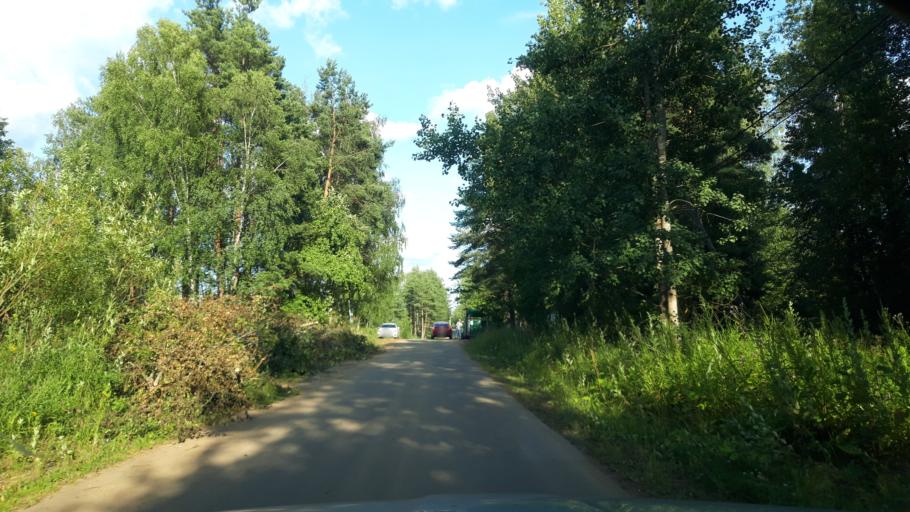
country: RU
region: Moskovskaya
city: Povarovo
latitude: 56.0618
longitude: 37.0865
